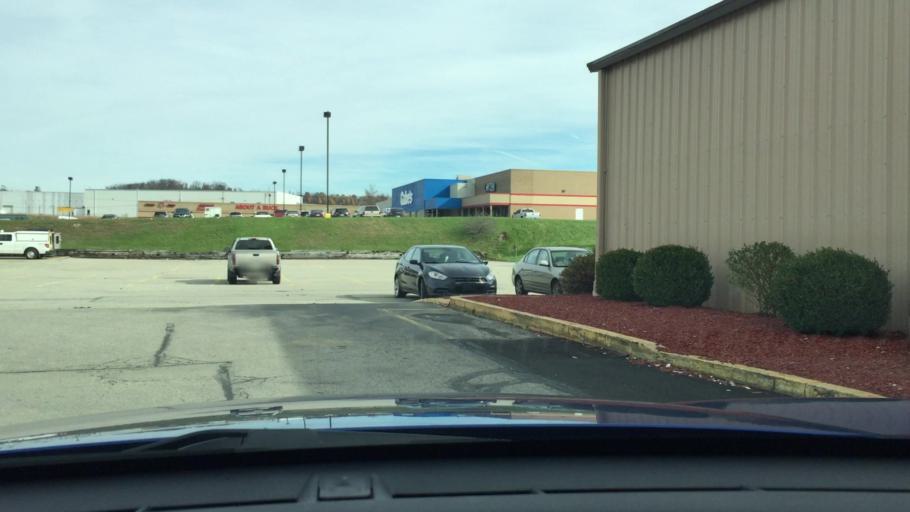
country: US
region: Pennsylvania
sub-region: Westmoreland County
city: Lynnwood-Pricedale
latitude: 40.1363
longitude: -79.8390
